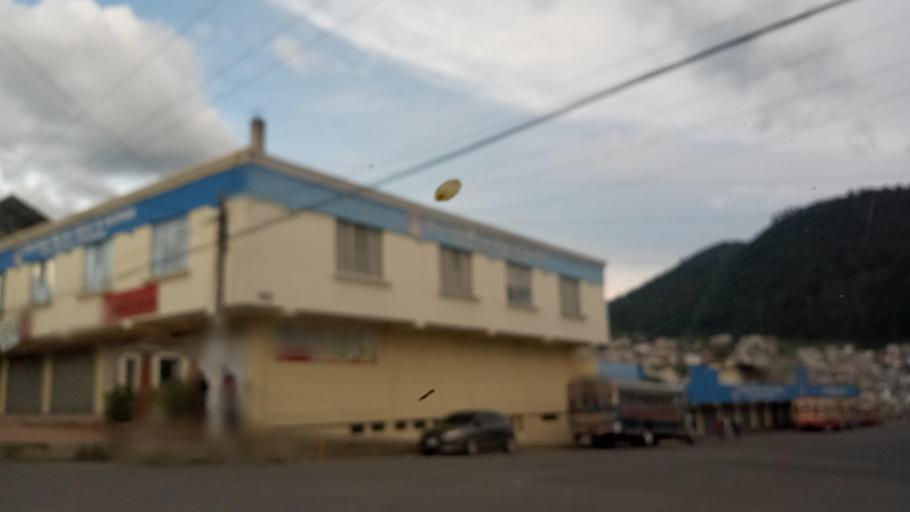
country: GT
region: Quetzaltenango
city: Quetzaltenango
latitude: 14.8371
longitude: -91.5126
